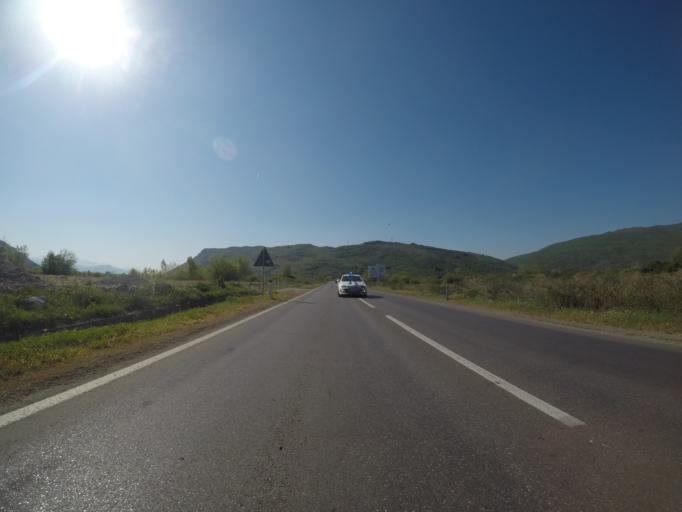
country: ME
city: Spuz
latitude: 42.4684
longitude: 19.1743
